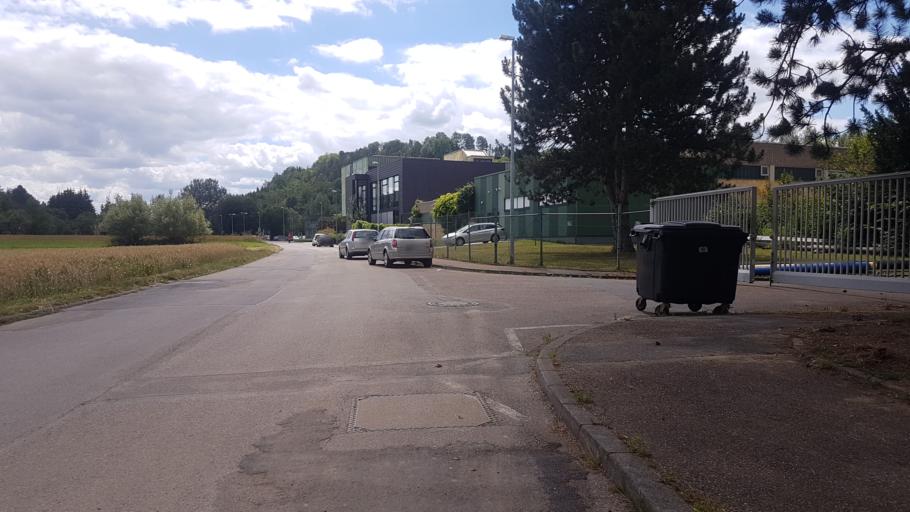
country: DE
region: Baden-Wuerttemberg
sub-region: Regierungsbezirk Stuttgart
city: Bad Mergentheim
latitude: 49.4792
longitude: 9.7684
